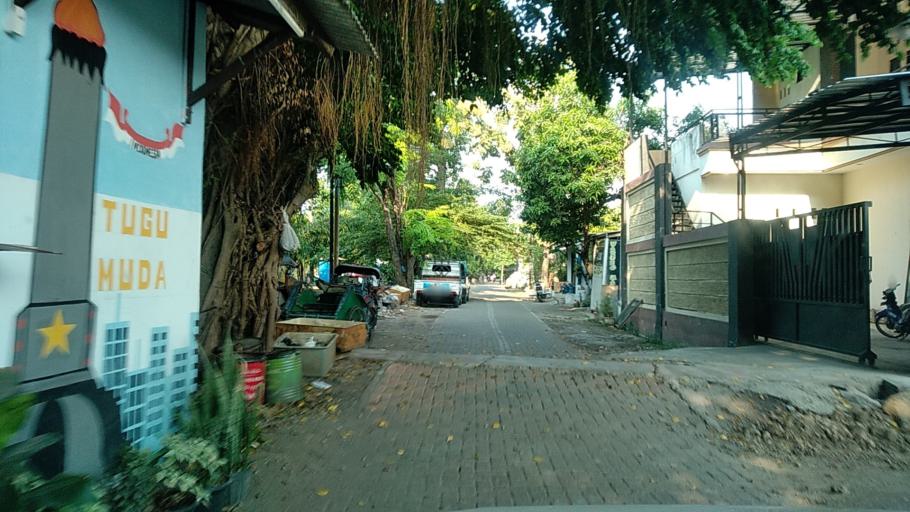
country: ID
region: Central Java
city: Semarang
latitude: -6.9655
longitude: 110.4043
